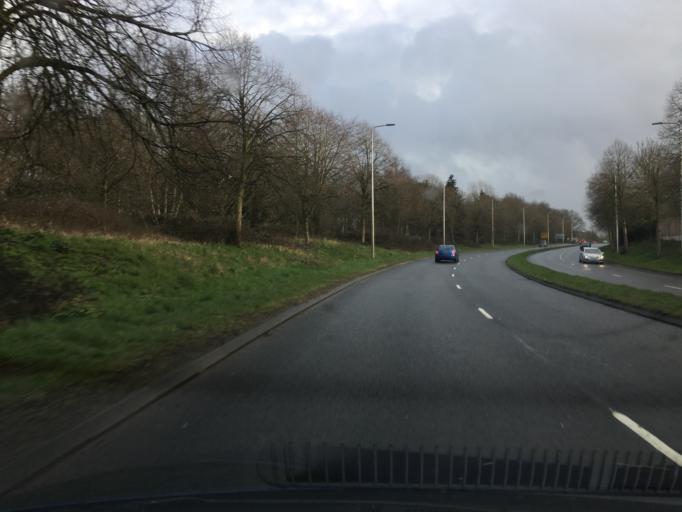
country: GB
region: England
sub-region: Bracknell Forest
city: Bracknell
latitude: 51.4003
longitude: -0.7621
